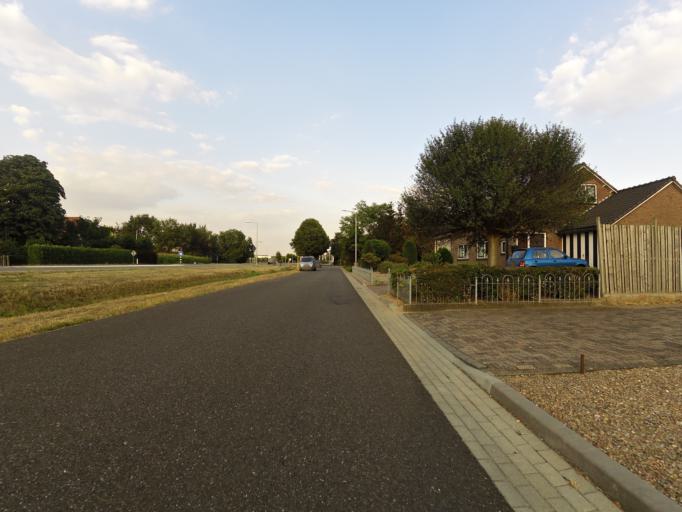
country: NL
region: Gelderland
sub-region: Gemeente Groesbeek
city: Berg en Dal
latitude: 51.8789
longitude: 5.9440
